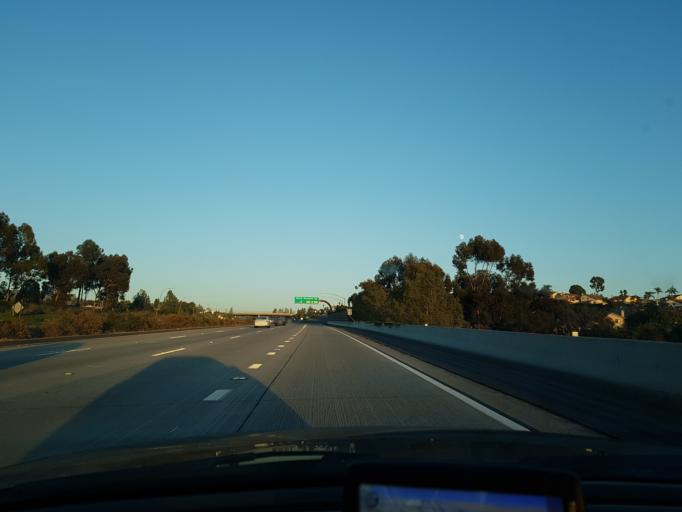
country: US
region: California
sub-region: San Diego County
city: Fairbanks Ranch
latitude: 32.9532
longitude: -117.1370
